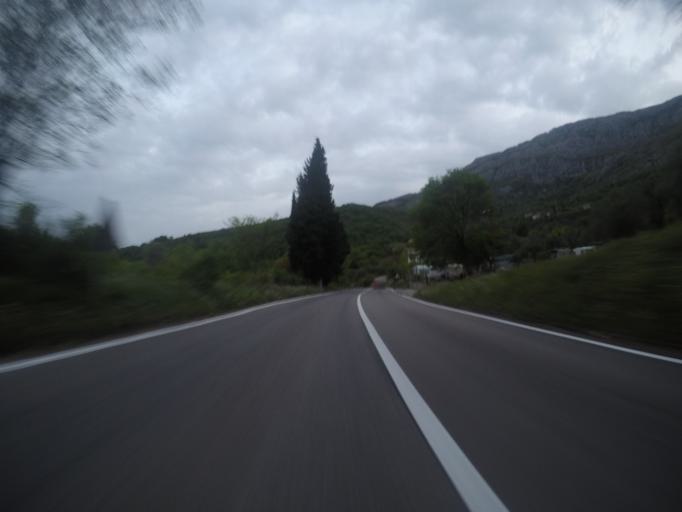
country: ME
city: Petrovac na Moru
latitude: 42.1971
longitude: 18.9786
